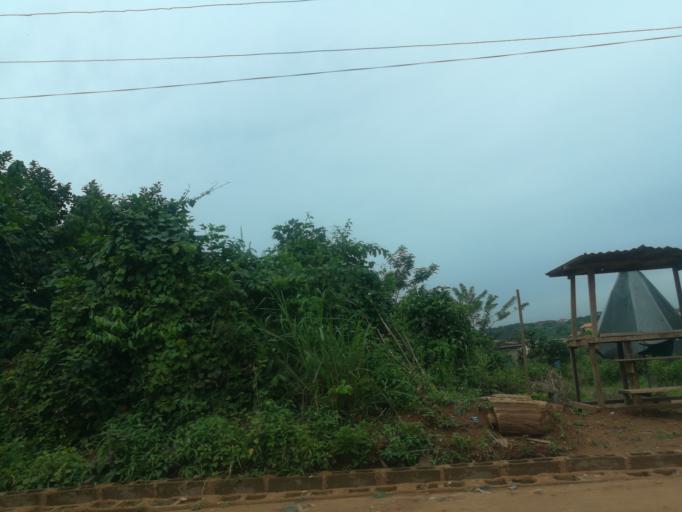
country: NG
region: Oyo
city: Ibadan
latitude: 7.3218
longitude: 3.8876
